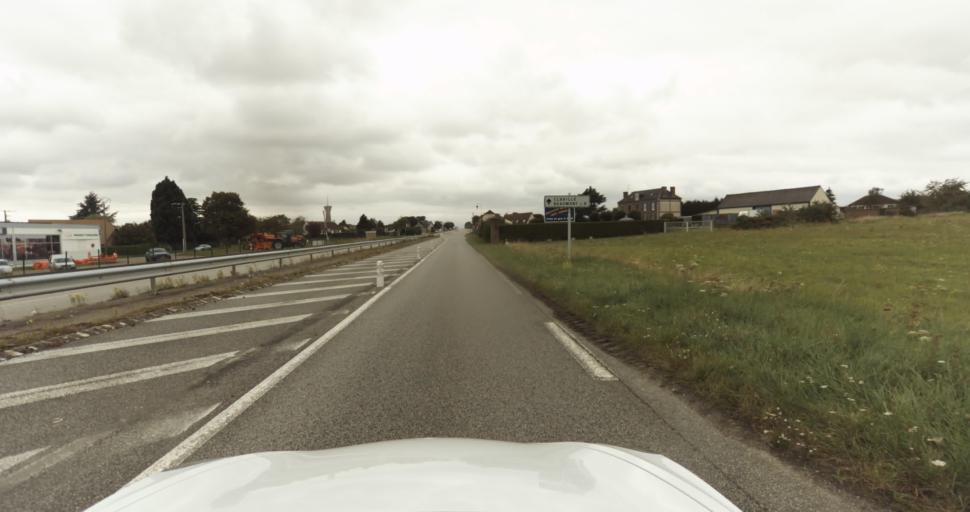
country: FR
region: Haute-Normandie
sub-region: Departement de l'Eure
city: Saint-Sebastien-de-Morsent
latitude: 49.0313
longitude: 1.1007
